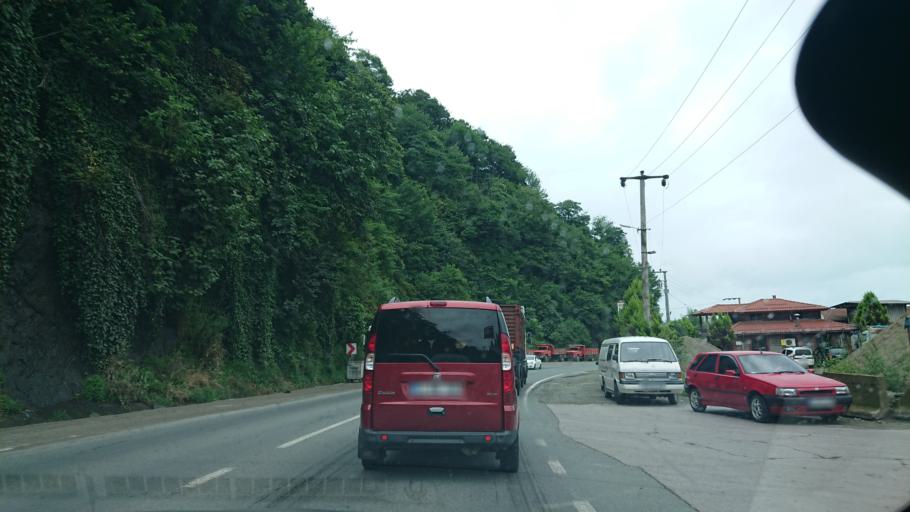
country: TR
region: Rize
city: Gundogdu
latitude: 41.0355
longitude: 40.5791
